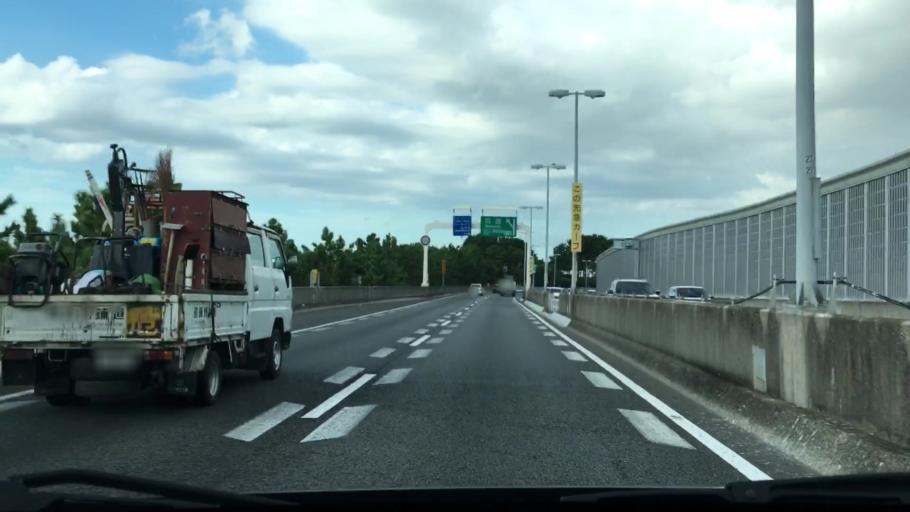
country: JP
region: Fukuoka
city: Fukuoka-shi
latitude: 33.5912
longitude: 130.3456
